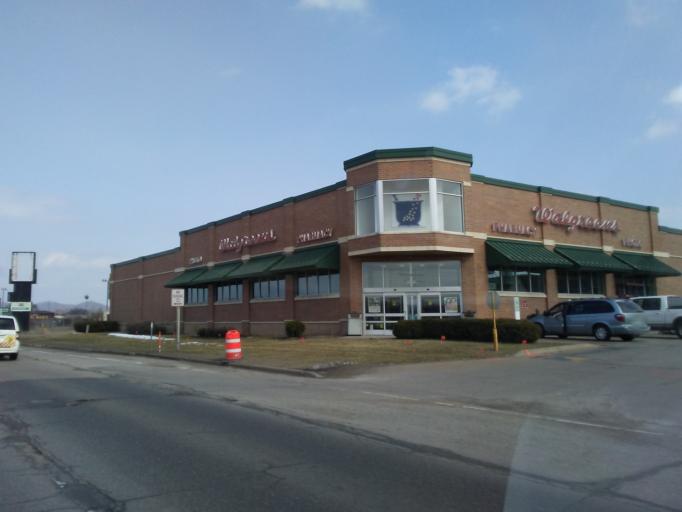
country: US
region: Wisconsin
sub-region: La Crosse County
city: North La Crosse
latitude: 43.8598
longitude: -91.2414
